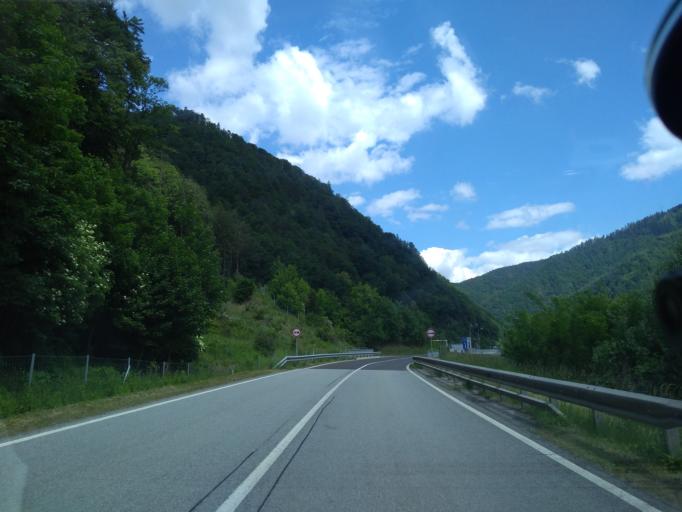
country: AT
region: Styria
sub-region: Politischer Bezirk Bruck-Muerzzuschlag
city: Pernegg an der Mur
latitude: 47.3776
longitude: 15.3046
